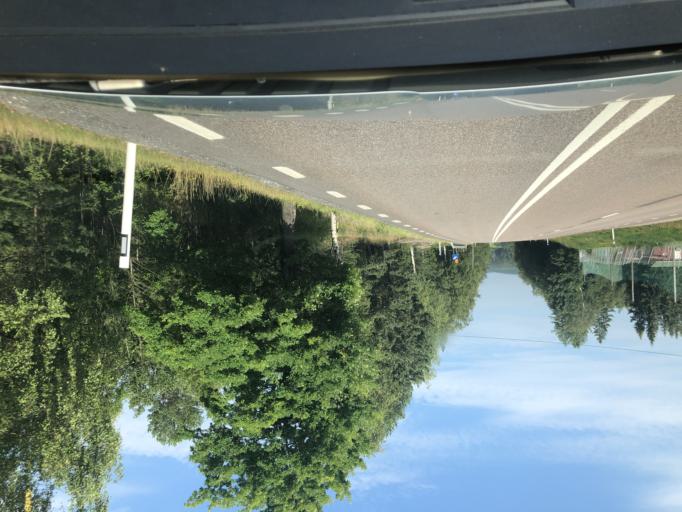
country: SE
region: Vaesternorrland
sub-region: Kramfors Kommun
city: Kramfors
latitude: 62.8142
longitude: 17.8655
